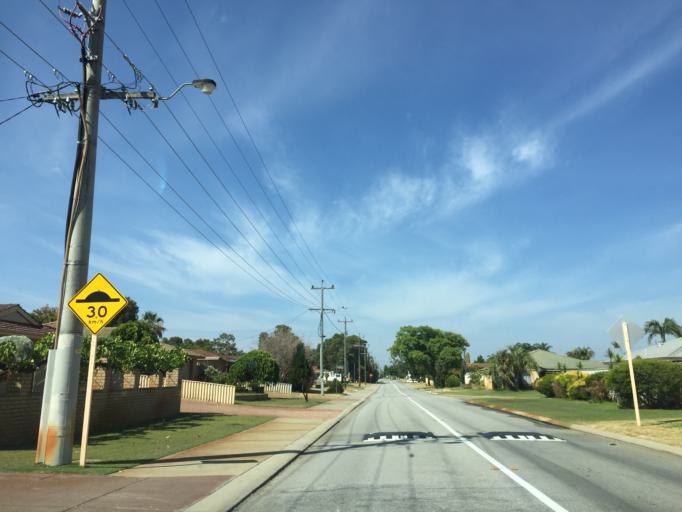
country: AU
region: Western Australia
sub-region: Gosnells
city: Thornlie
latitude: -32.0794
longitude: 115.9636
